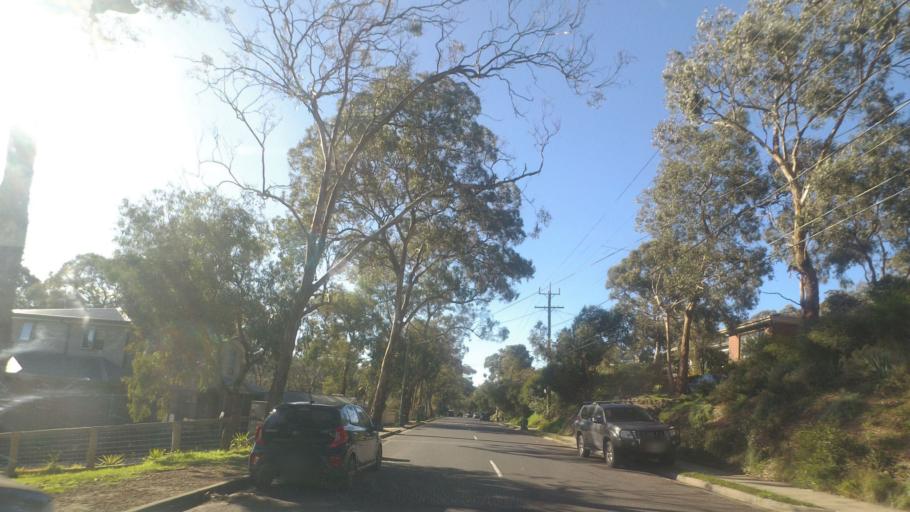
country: AU
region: Victoria
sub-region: Banyule
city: Montmorency
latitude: -37.7169
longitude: 145.1327
